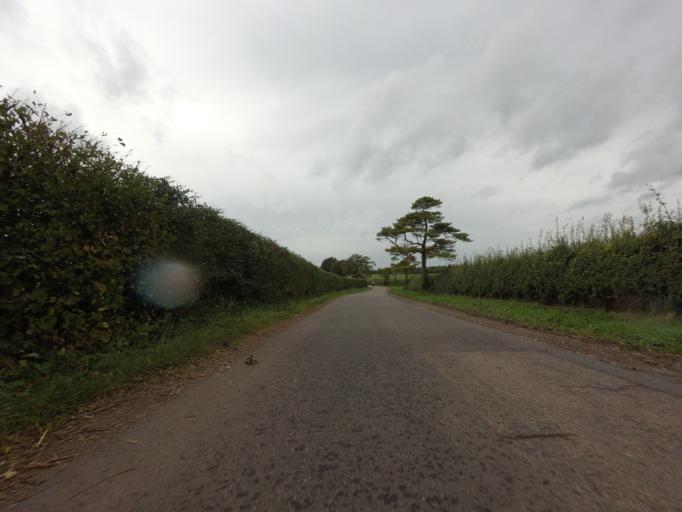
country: GB
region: England
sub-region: Cambridgeshire
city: Duxford
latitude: 52.0609
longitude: 0.1166
